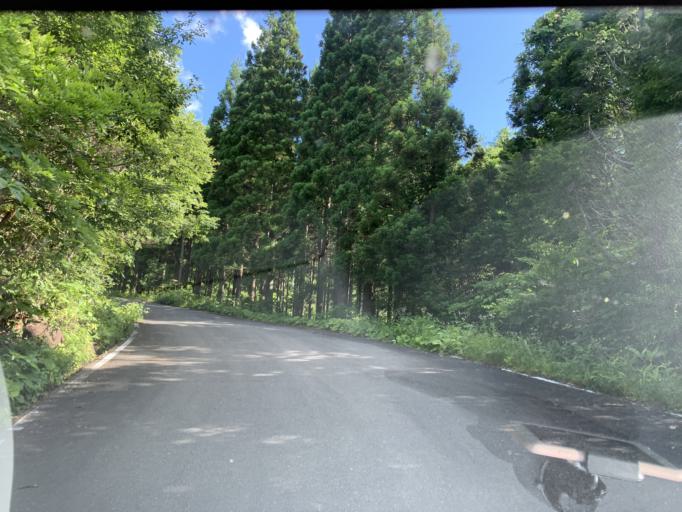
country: JP
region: Iwate
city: Ichinoseki
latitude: 38.8926
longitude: 140.9066
